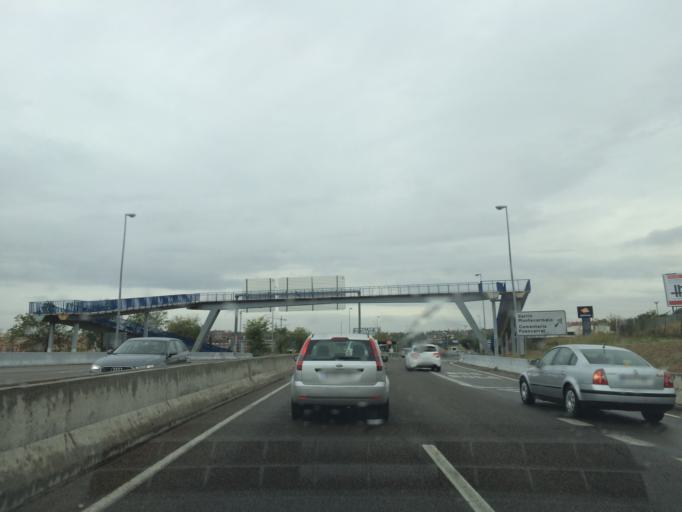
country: ES
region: Madrid
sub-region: Provincia de Madrid
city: Las Tablas
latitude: 40.4983
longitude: -3.6999
